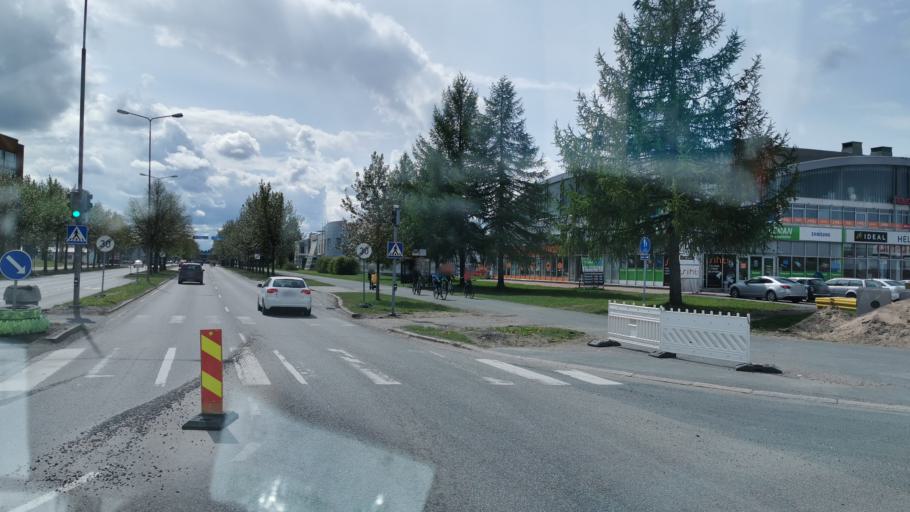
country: FI
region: Northern Ostrobothnia
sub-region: Oulu
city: Oulu
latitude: 65.0006
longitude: 25.4638
